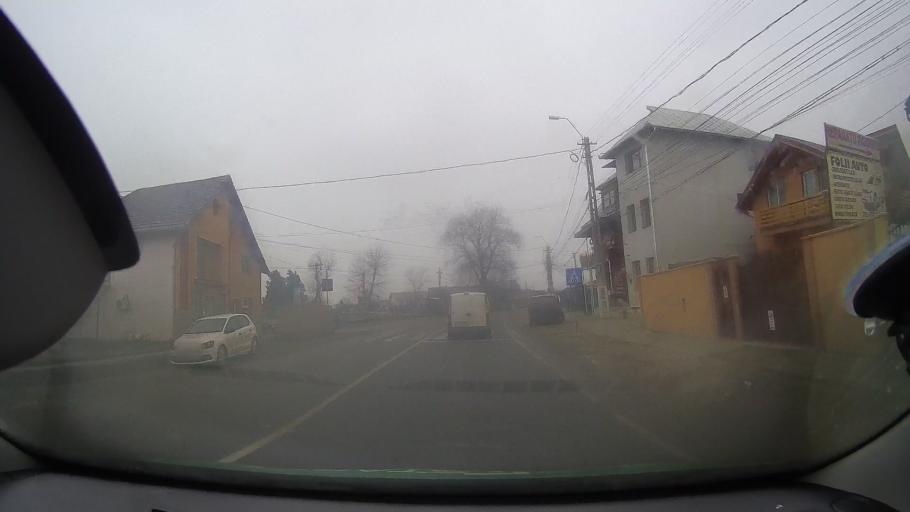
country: RO
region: Cluj
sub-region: Comuna Mihai Viteazu
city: Mihai Viteazu
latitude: 46.5406
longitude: 23.7629
